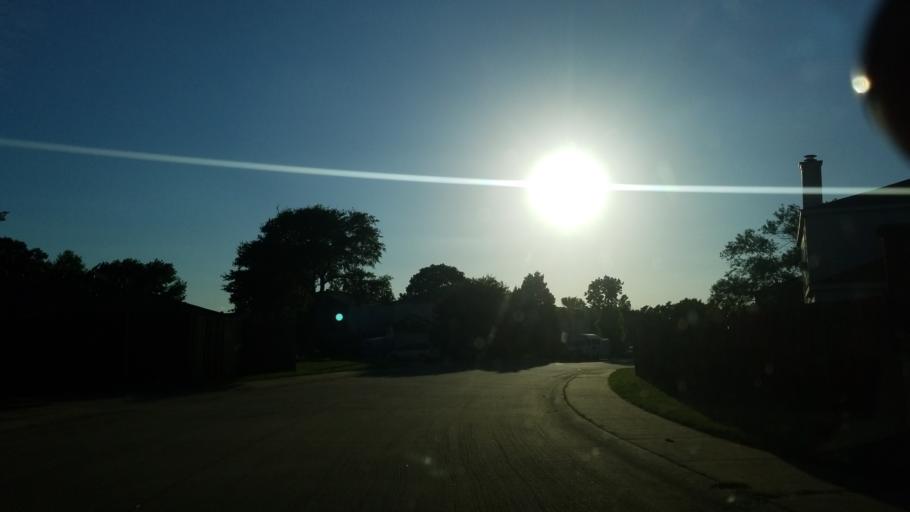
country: US
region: Texas
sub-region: Dallas County
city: Balch Springs
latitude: 32.7818
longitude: -96.6975
